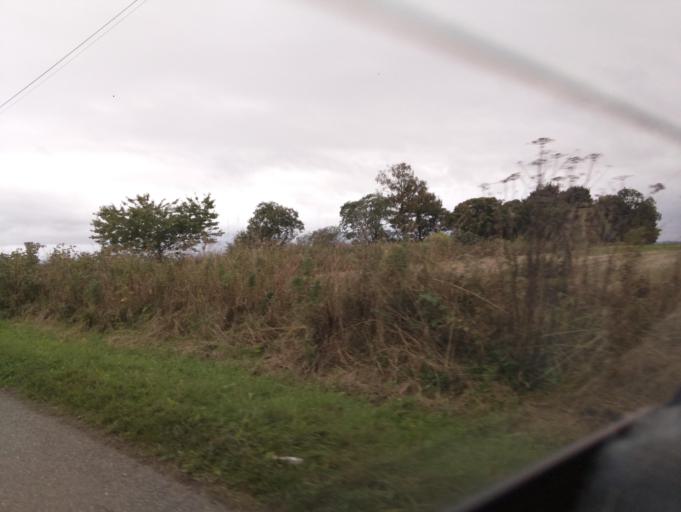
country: GB
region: Scotland
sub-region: Perth and Kinross
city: Milnathort
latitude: 56.2347
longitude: -3.3647
